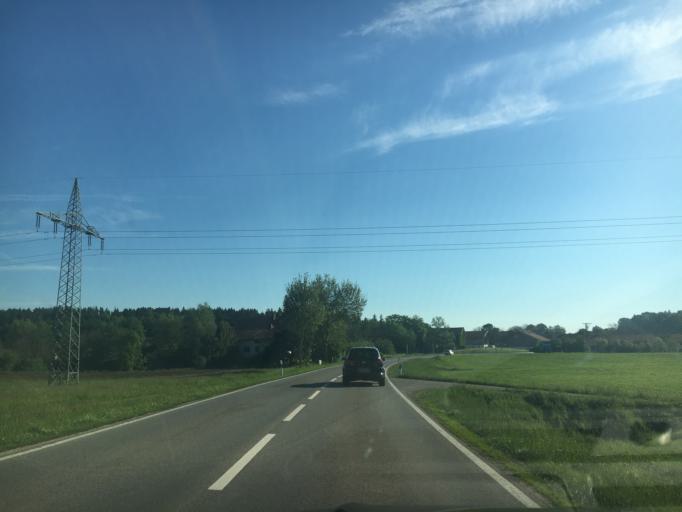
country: DE
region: Bavaria
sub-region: Upper Bavaria
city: Chieming
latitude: 47.8997
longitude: 12.5469
